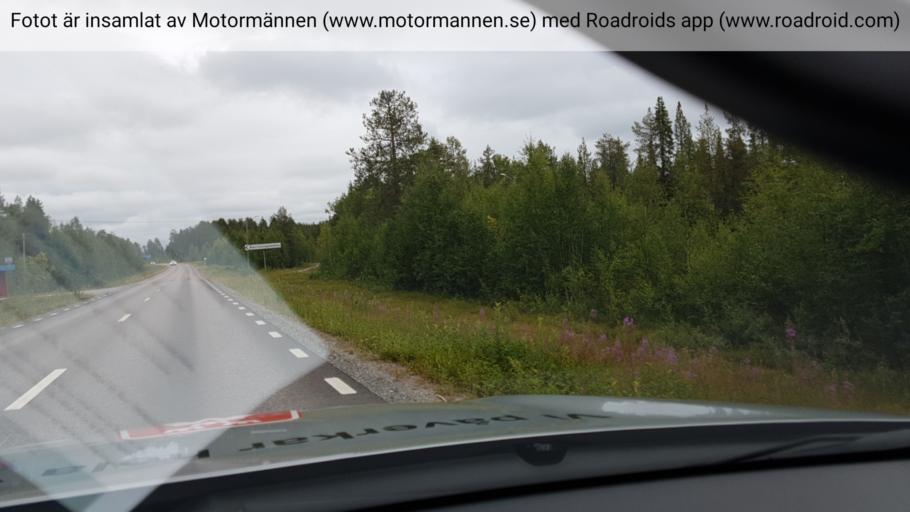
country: SE
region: Norrbotten
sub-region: Gallivare Kommun
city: Gaellivare
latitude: 67.0687
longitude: 21.3121
